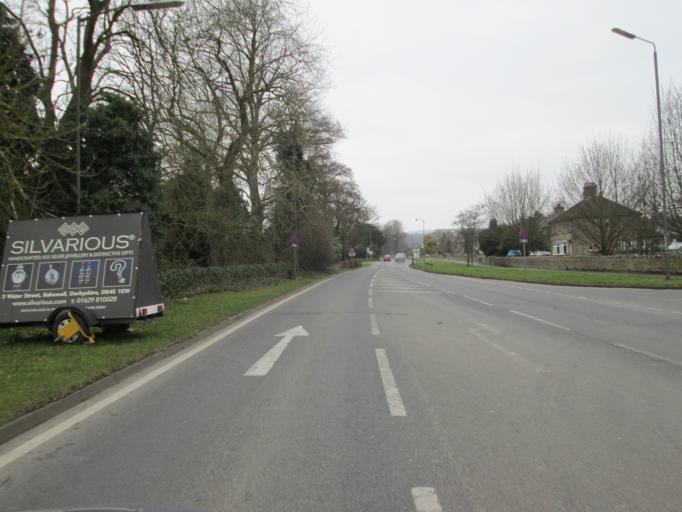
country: GB
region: England
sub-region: Derbyshire
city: Bakewell
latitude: 53.2064
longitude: -1.6681
